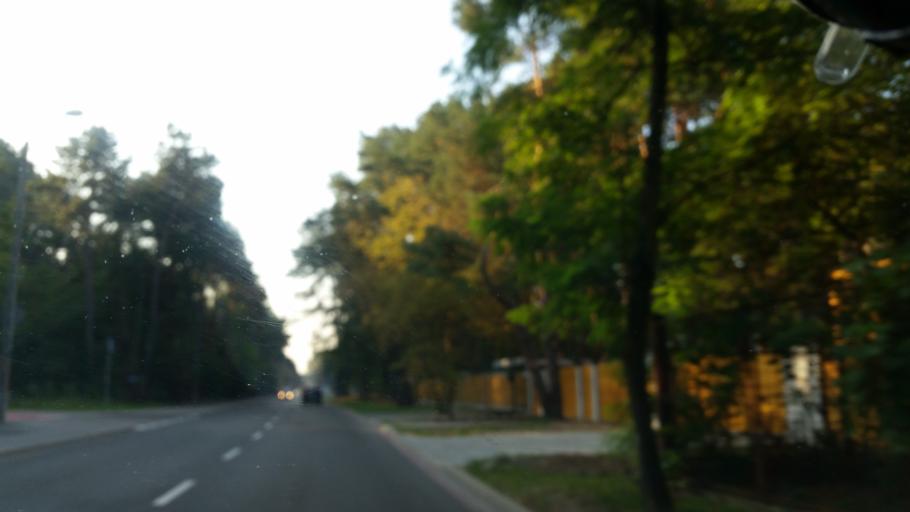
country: PL
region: Masovian Voivodeship
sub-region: Powiat otwocki
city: Jozefow
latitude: 52.1400
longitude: 21.2159
